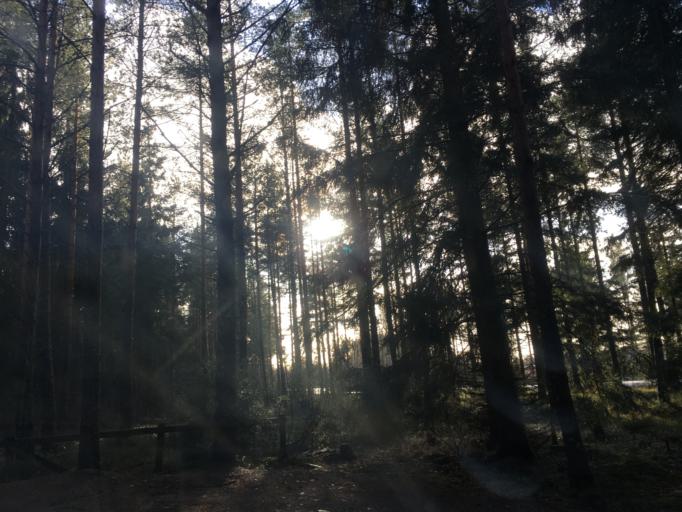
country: FI
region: Varsinais-Suomi
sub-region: Turku
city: Raisio
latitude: 60.5115
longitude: 22.1592
